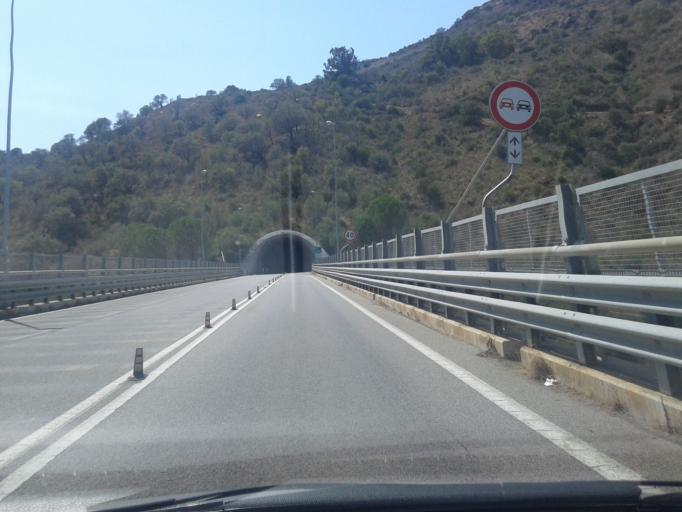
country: IT
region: Sicily
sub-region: Palermo
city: Pollina
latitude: 38.0091
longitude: 14.1001
